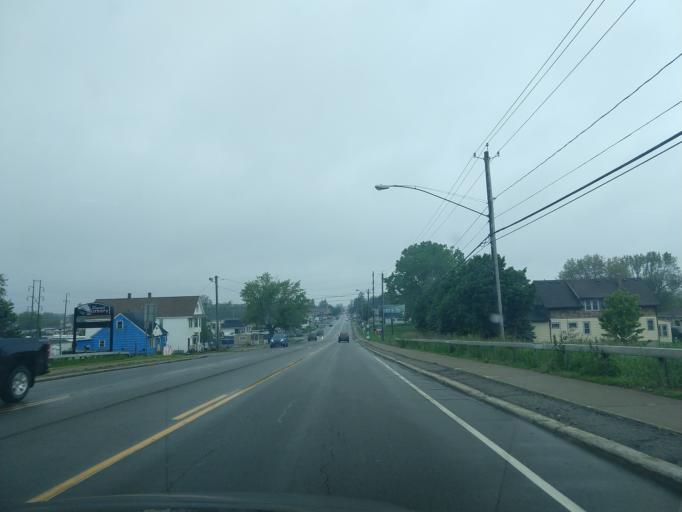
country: US
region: New York
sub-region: Erie County
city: Blasdell
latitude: 42.8039
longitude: -78.8239
